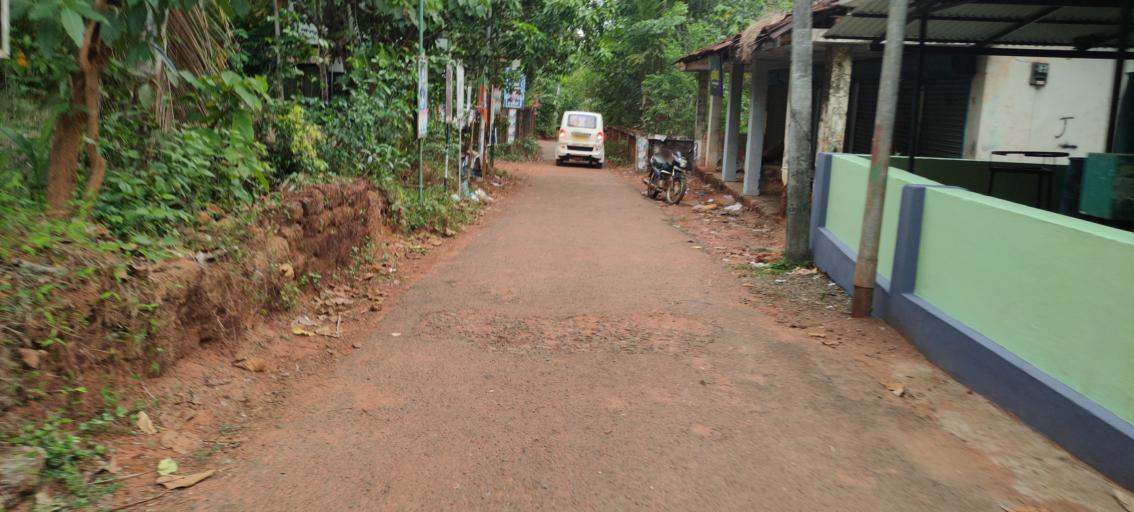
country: IN
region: Kerala
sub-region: Malappuram
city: Ponnani
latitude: 10.7686
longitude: 76.0324
